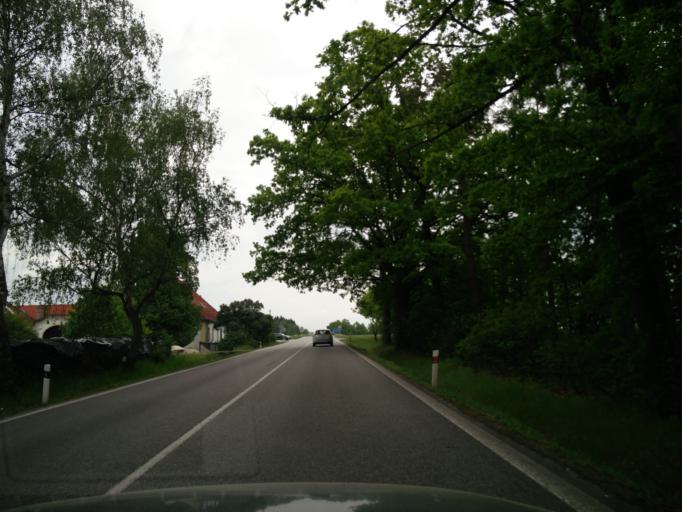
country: CZ
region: Jihocesky
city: Netolice
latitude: 49.0852
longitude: 14.2632
